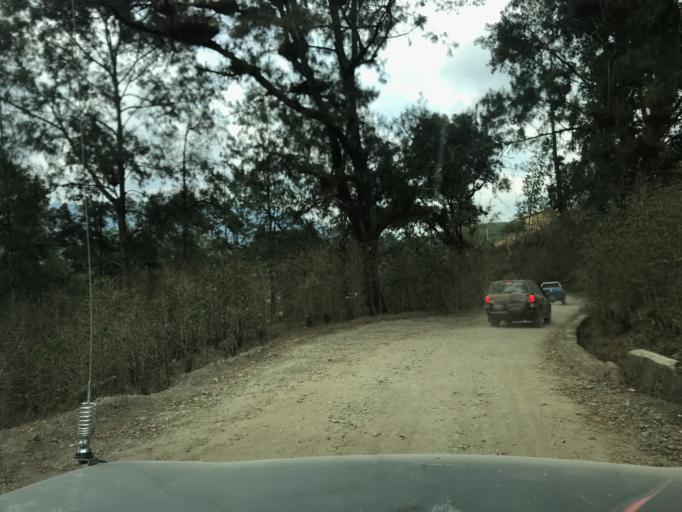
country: TL
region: Ermera
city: Gleno
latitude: -8.8227
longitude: 125.4319
